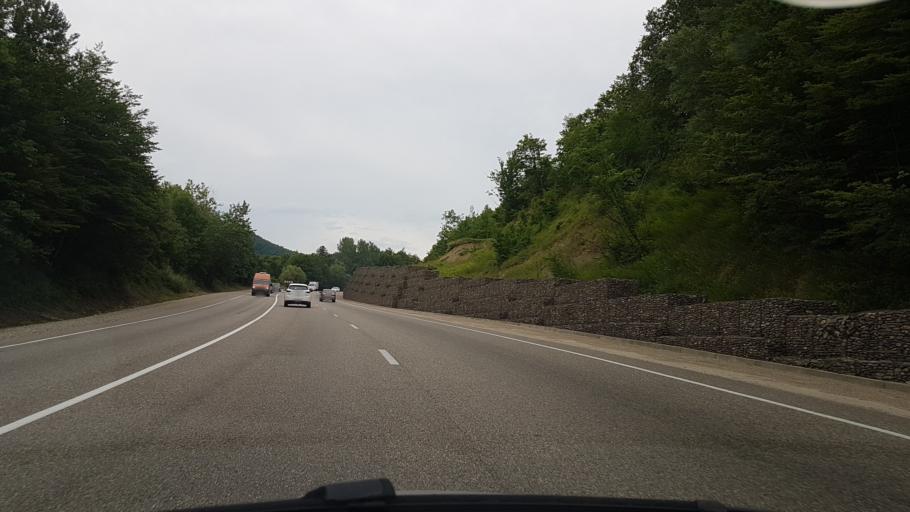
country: RU
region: Krasnodarskiy
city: Goryachiy Klyuch
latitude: 44.5095
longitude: 38.9095
